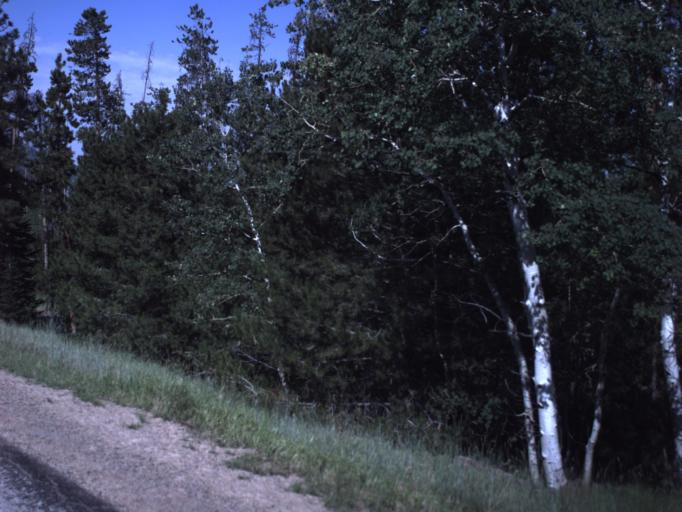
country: US
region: Utah
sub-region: Daggett County
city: Manila
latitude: 40.8561
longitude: -109.5607
